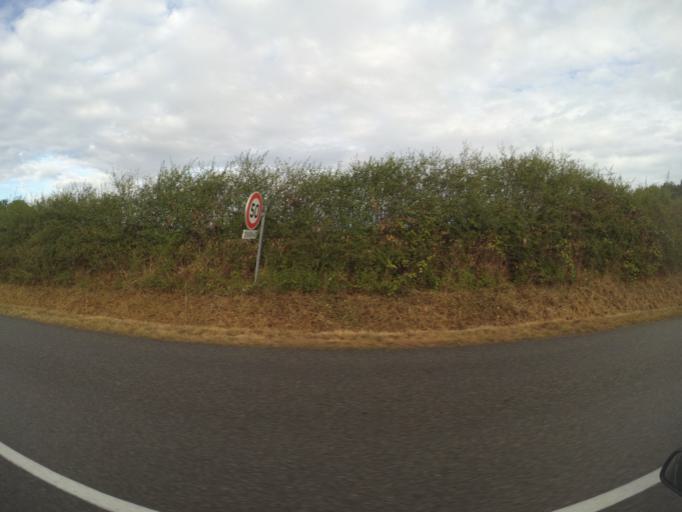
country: FR
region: Pays de la Loire
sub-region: Departement de la Loire-Atlantique
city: La Planche
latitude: 47.0125
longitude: -1.4253
